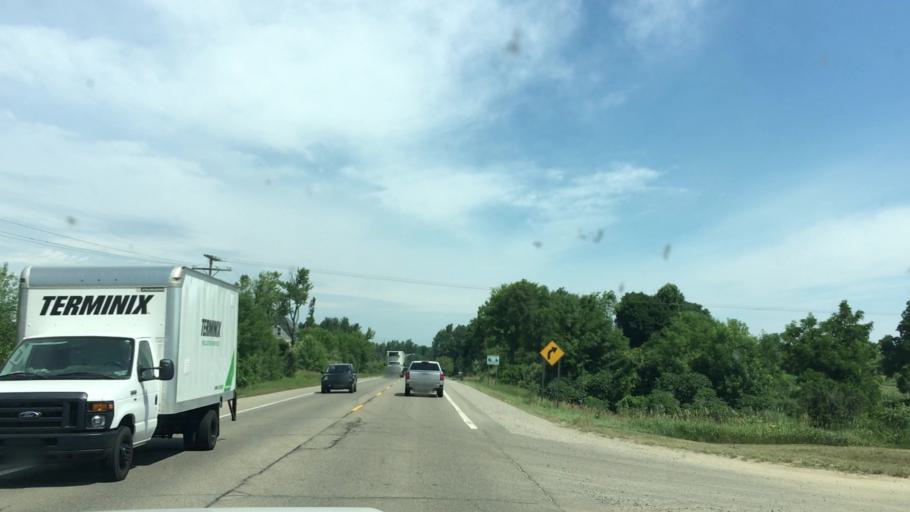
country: US
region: Michigan
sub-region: Lapeer County
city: Imlay City
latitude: 43.0801
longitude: -83.0757
